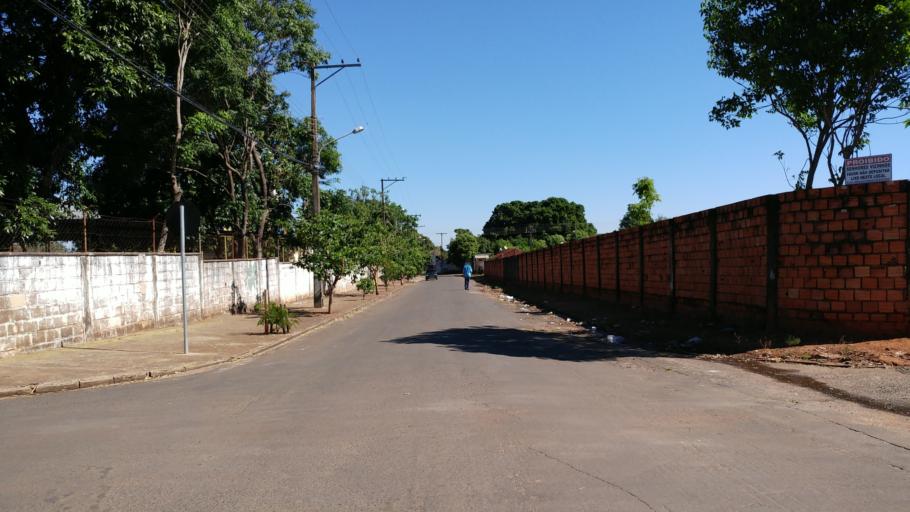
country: BR
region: Sao Paulo
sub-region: Paraguacu Paulista
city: Paraguacu Paulista
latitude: -22.4339
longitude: -50.5835
